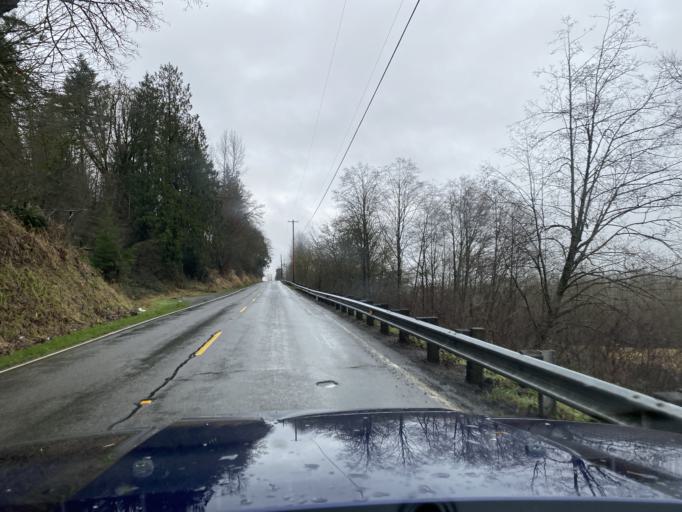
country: US
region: Washington
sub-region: King County
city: Duvall
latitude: 47.7795
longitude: -121.9990
